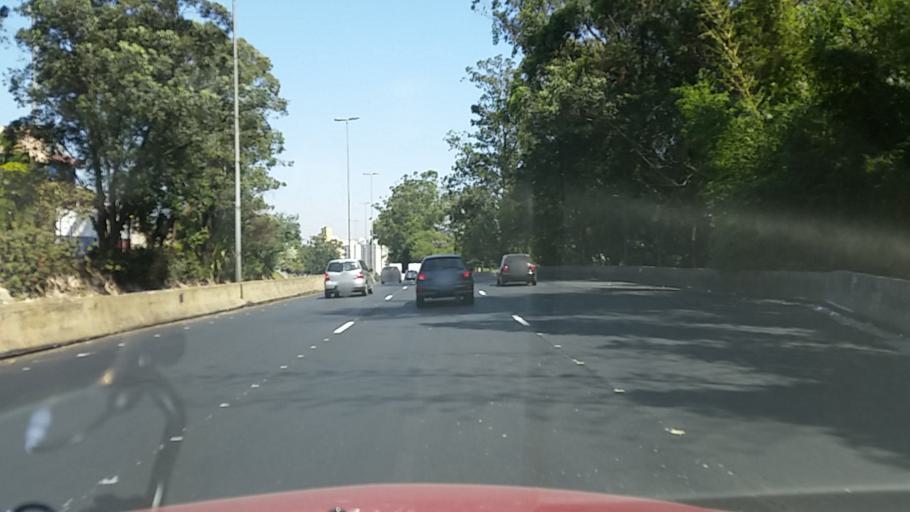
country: BR
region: Sao Paulo
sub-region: Taboao Da Serra
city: Taboao da Serra
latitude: -23.5821
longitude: -46.7324
